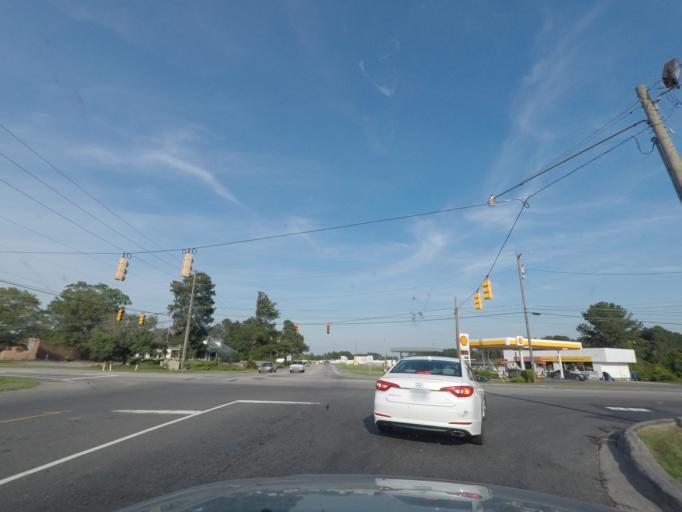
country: US
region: North Carolina
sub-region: Granville County
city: Oxford
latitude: 36.2951
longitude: -78.6022
